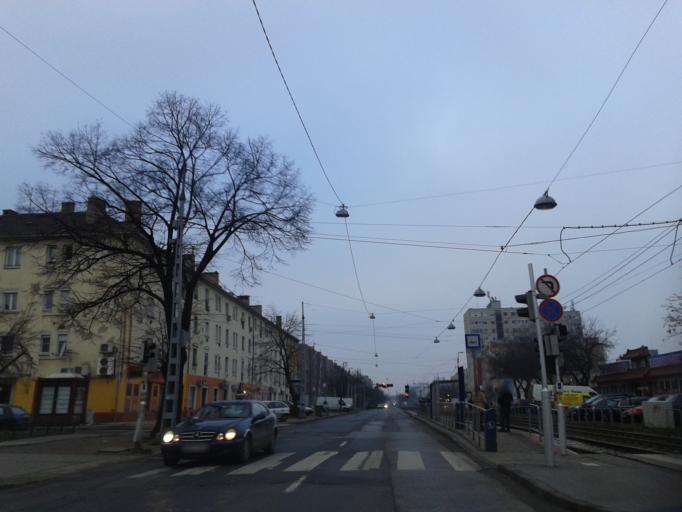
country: HU
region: Budapest
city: Budapest XIV. keruelet
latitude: 47.5116
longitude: 19.1254
